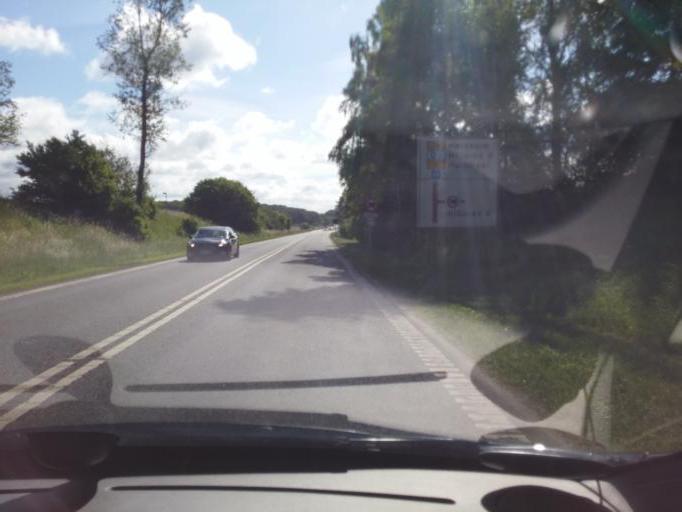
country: DK
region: Capital Region
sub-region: Hillerod Kommune
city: Hillerod
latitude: 55.9557
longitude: 12.2564
